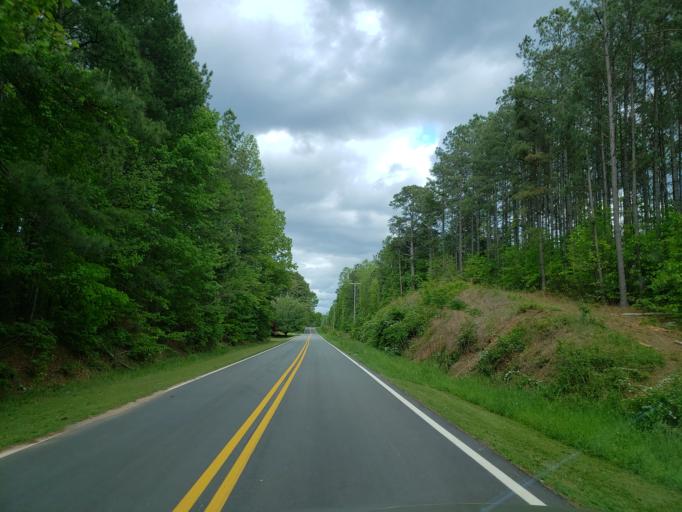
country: US
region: Georgia
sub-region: Haralson County
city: Tallapoosa
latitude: 33.8636
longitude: -85.3361
